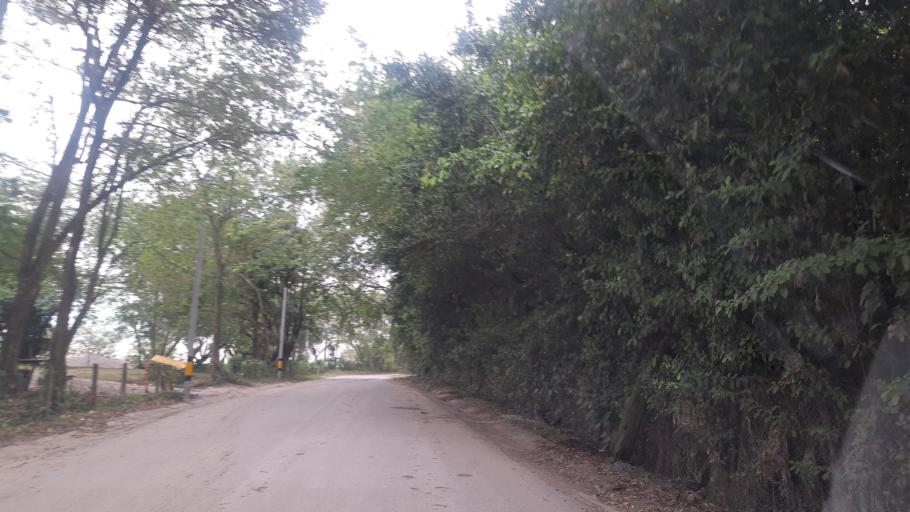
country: CO
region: Antioquia
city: Puerto Triunfo
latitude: 5.8779
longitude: -74.6355
